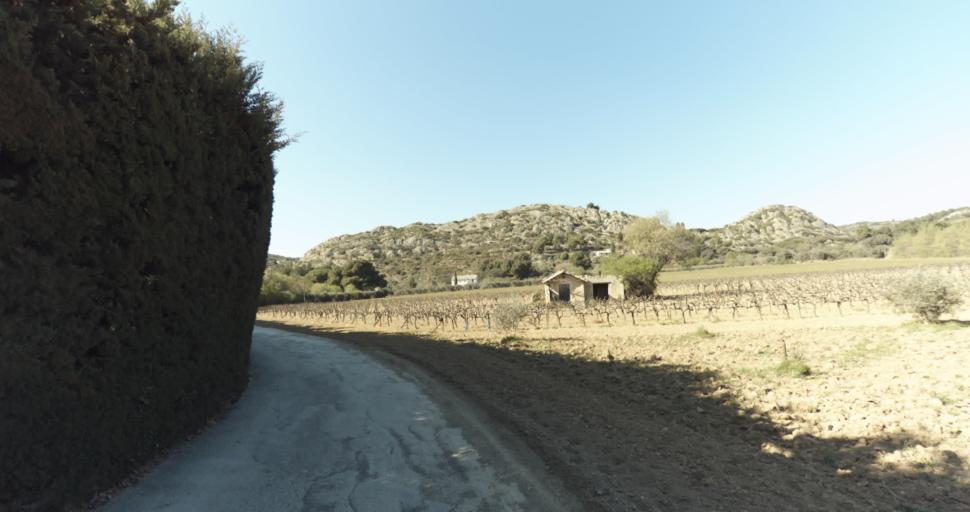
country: FR
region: Provence-Alpes-Cote d'Azur
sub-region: Departement des Bouches-du-Rhone
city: Pelissanne
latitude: 43.6398
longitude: 5.1419
